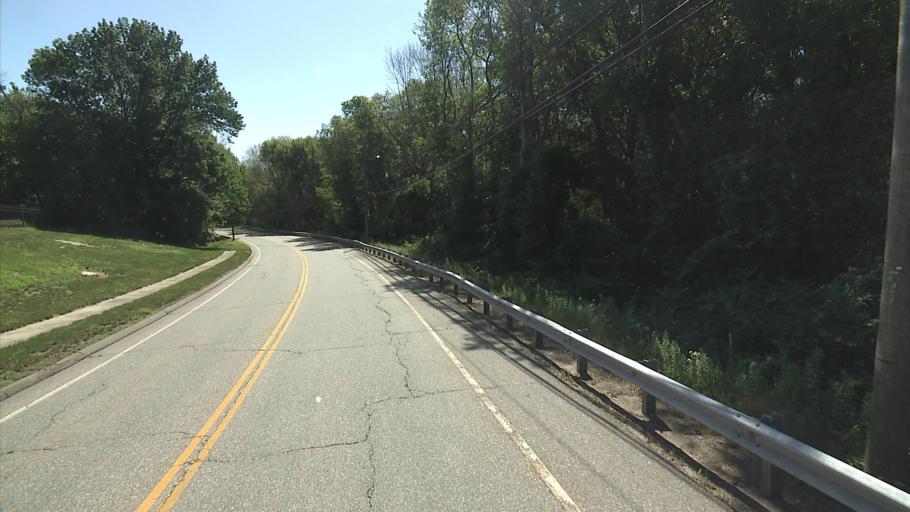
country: US
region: Connecticut
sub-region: New London County
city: Colchester
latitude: 41.5810
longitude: -72.3145
